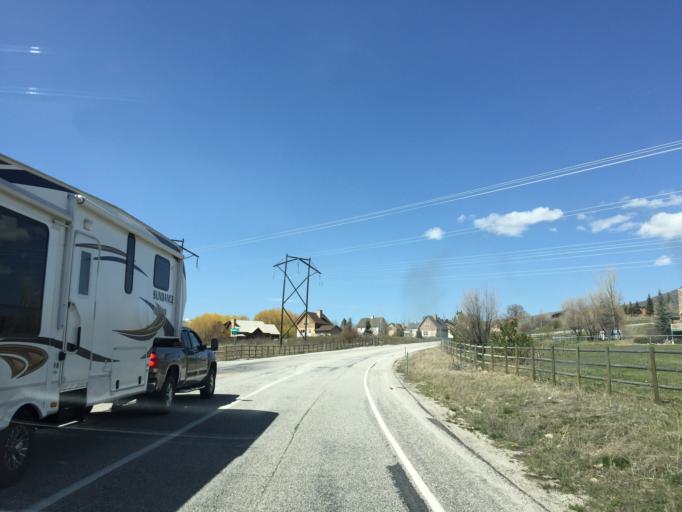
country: US
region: Utah
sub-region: Weber County
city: Wolf Creek
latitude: 41.3203
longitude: -111.8293
